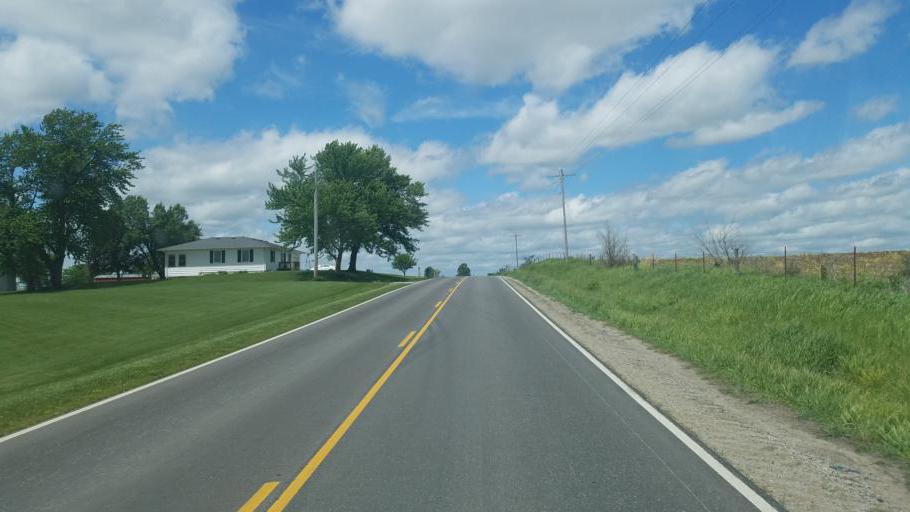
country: US
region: Iowa
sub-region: Decatur County
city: Lamoni
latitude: 40.4869
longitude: -93.9936
